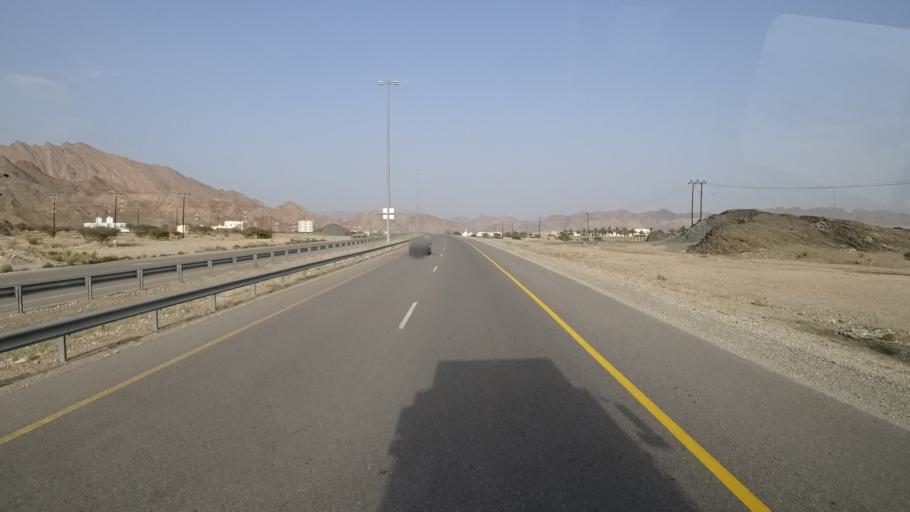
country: OM
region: Muhafazat Masqat
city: Muscat
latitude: 23.3390
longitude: 58.5971
